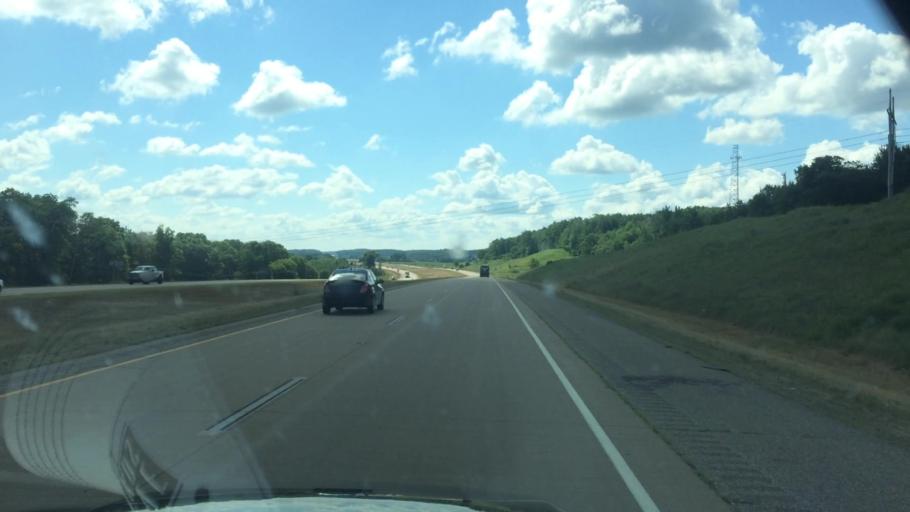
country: US
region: Wisconsin
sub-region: Portage County
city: Amherst
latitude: 44.4141
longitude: -89.2439
